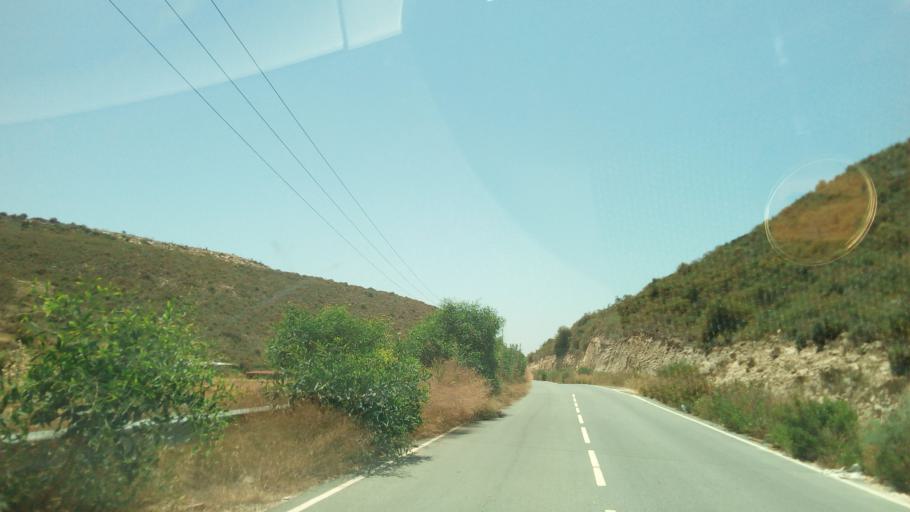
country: CY
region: Limassol
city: Ypsonas
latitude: 34.7371
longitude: 32.9472
